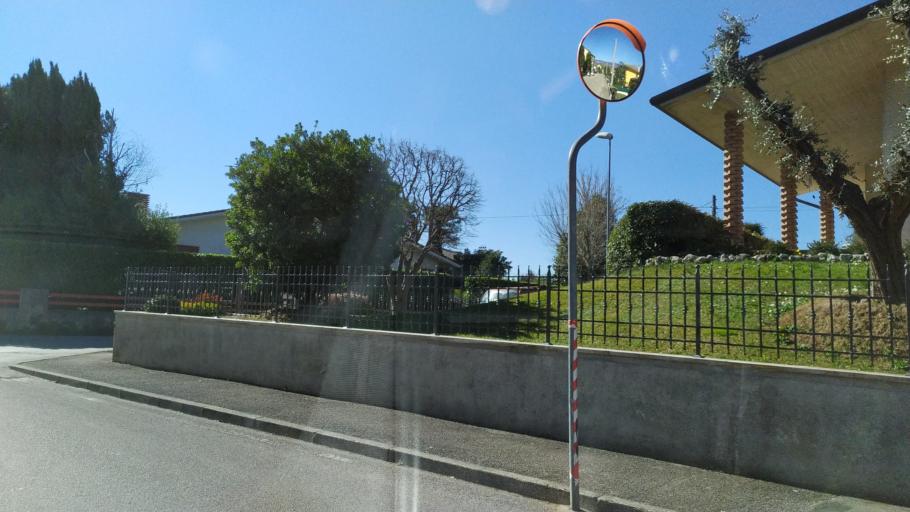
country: IT
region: Veneto
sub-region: Provincia di Vicenza
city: Breganze
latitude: 45.7022
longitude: 11.5665
